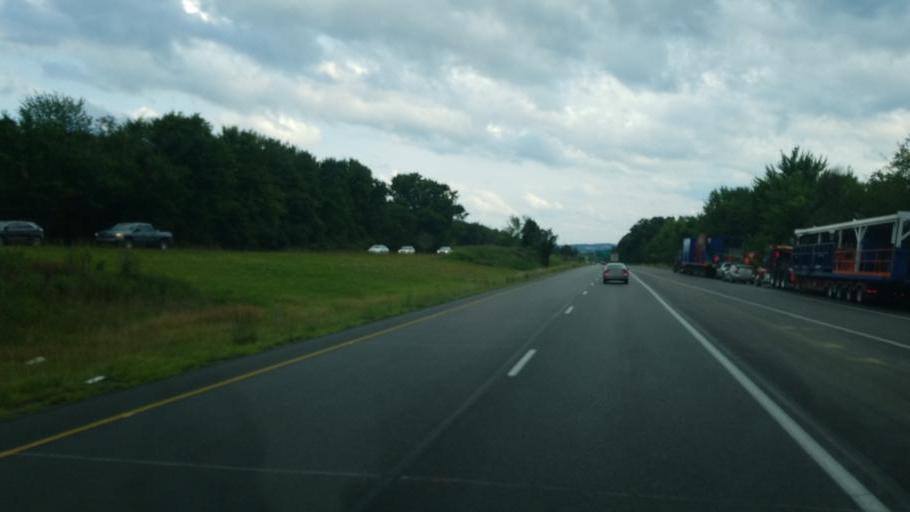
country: US
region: Pennsylvania
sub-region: Butler County
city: Fox Run
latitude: 40.7166
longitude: -80.1021
